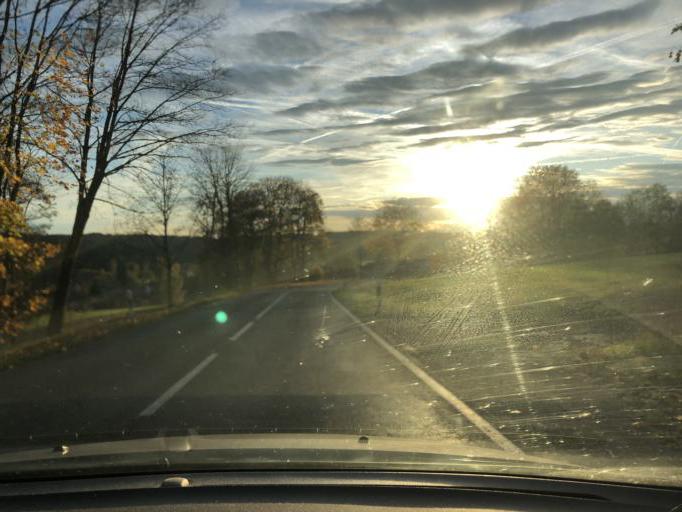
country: DE
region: Thuringia
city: Schleusingen
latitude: 50.4724
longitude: 10.7517
